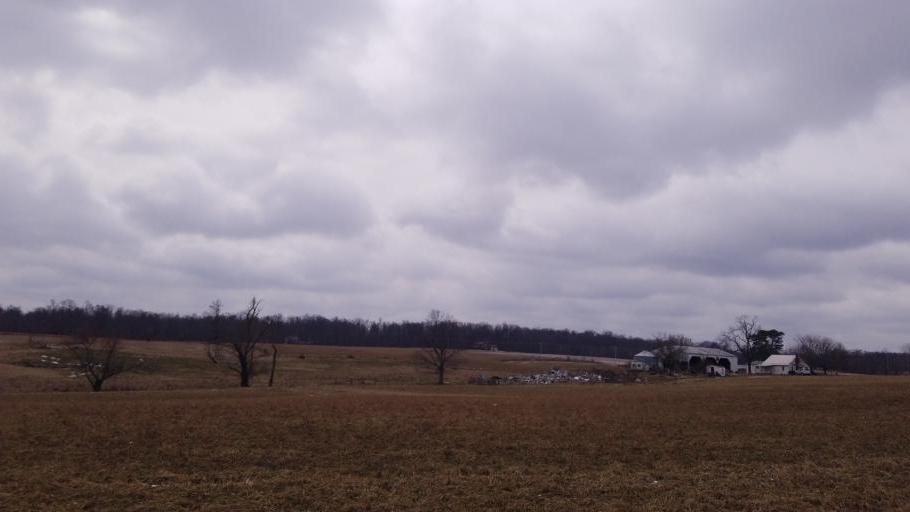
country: US
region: Ohio
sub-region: Crawford County
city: Galion
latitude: 40.6675
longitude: -82.7153
